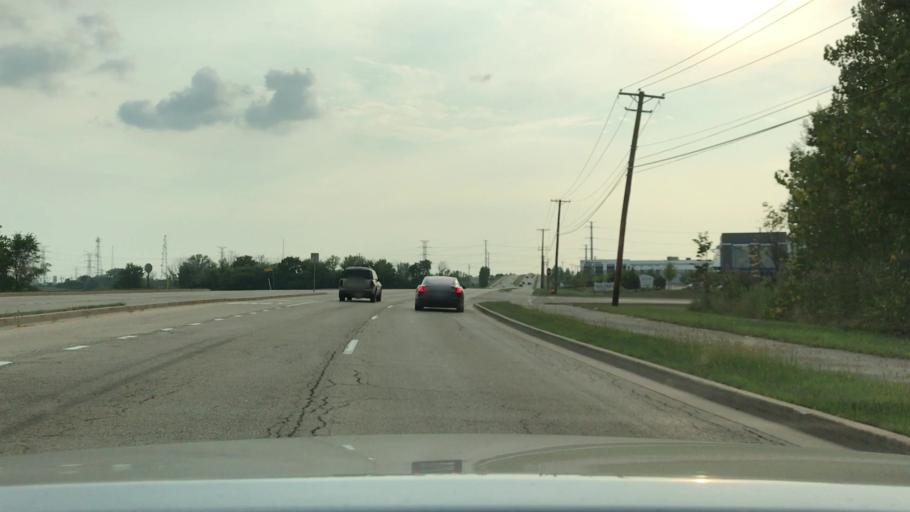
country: US
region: Illinois
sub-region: DuPage County
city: Warrenville
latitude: 41.8086
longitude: -88.2198
